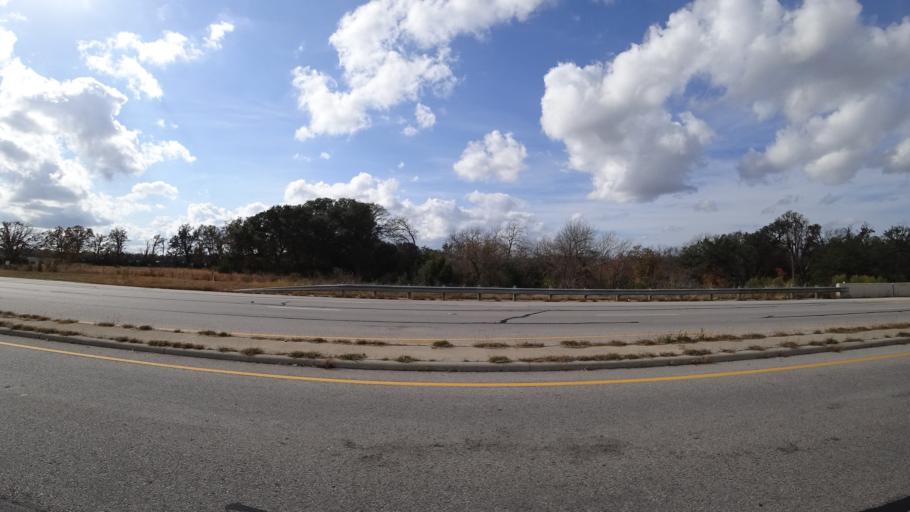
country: US
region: Texas
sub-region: Williamson County
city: Brushy Creek
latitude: 30.4828
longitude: -97.7197
